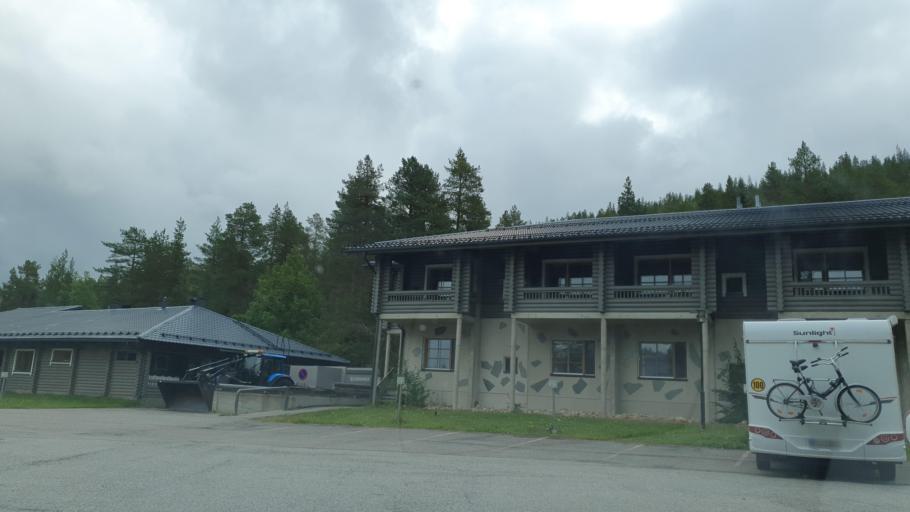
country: FI
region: Lapland
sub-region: Tunturi-Lappi
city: Kittilae
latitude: 67.8026
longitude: 24.7993
